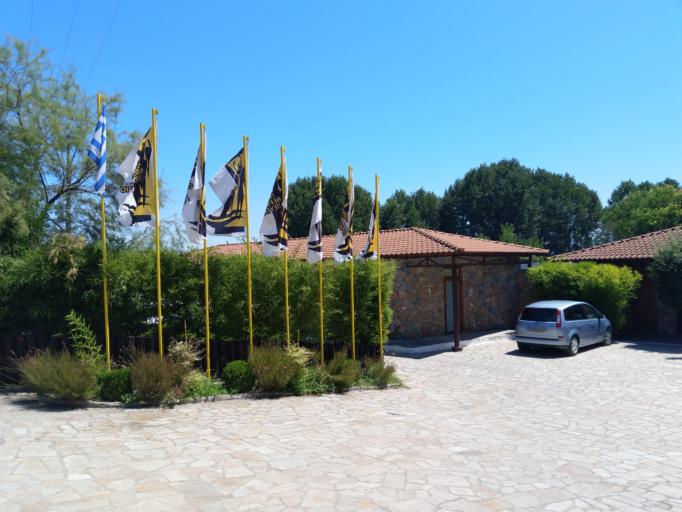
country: GR
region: East Macedonia and Thrace
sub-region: Nomos Kavalas
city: Krinides
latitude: 41.0115
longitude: 24.2559
